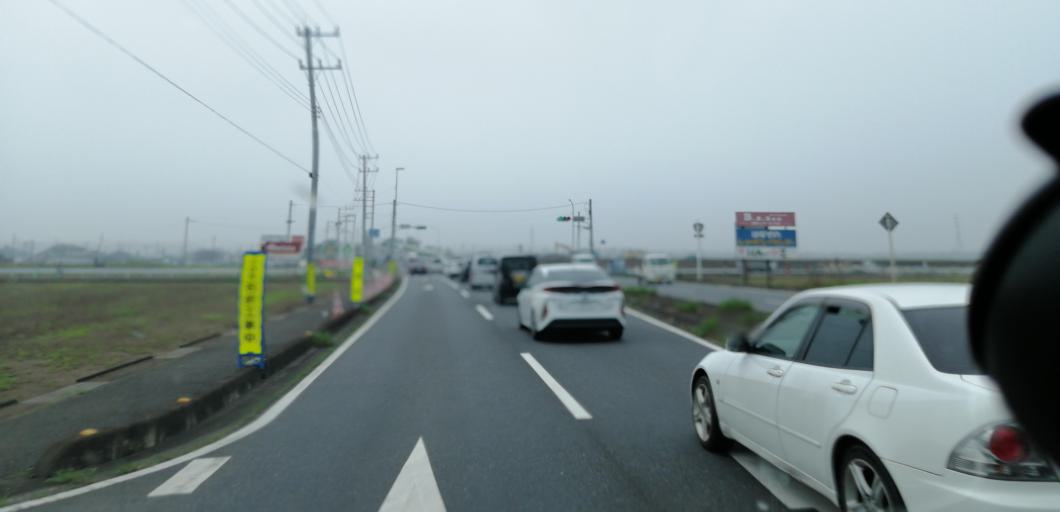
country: JP
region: Saitama
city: Yorii
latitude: 36.1363
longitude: 139.2524
